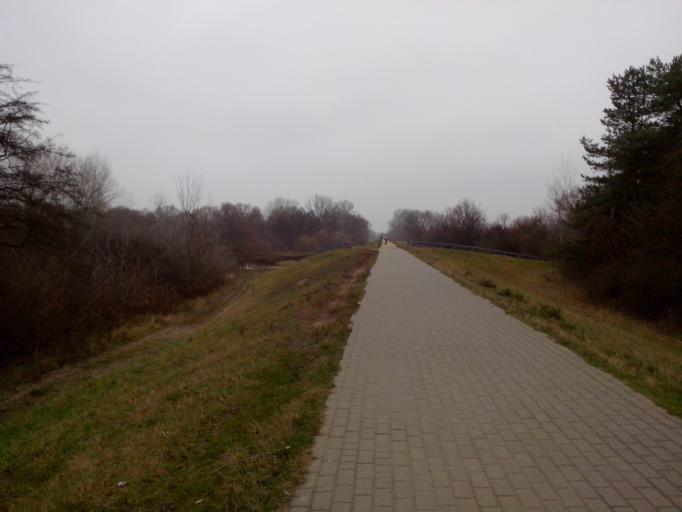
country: PL
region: Masovian Voivodeship
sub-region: Warszawa
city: Bielany
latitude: 52.3340
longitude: 20.9318
